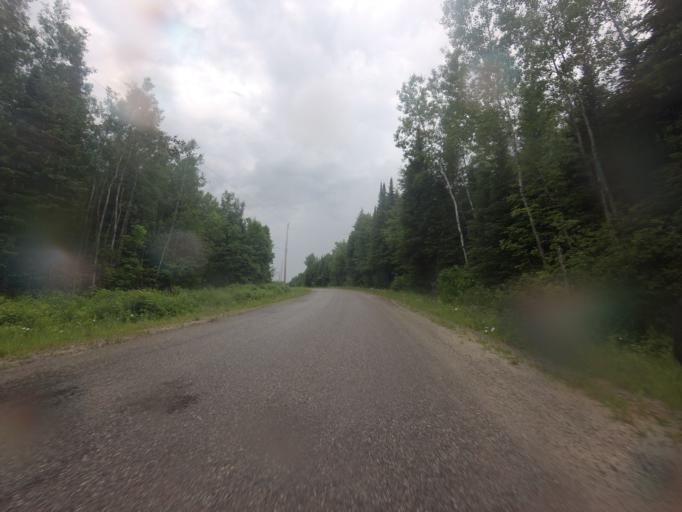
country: CA
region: Quebec
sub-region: Outaouais
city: Maniwaki
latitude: 46.4387
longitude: -75.9401
